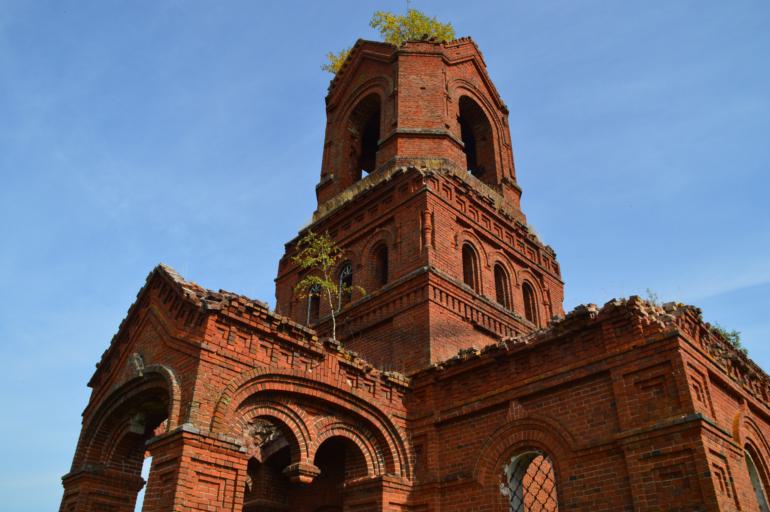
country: RU
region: Kirov
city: Dubrovka
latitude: 59.4608
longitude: 51.2556
